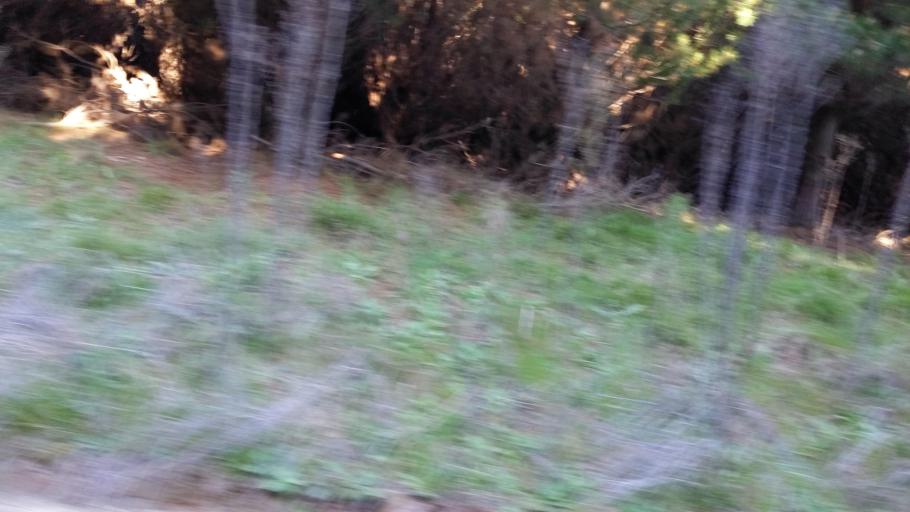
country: AU
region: New South Wales
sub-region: Blayney
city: Millthorpe
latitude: -33.3994
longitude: 149.3132
